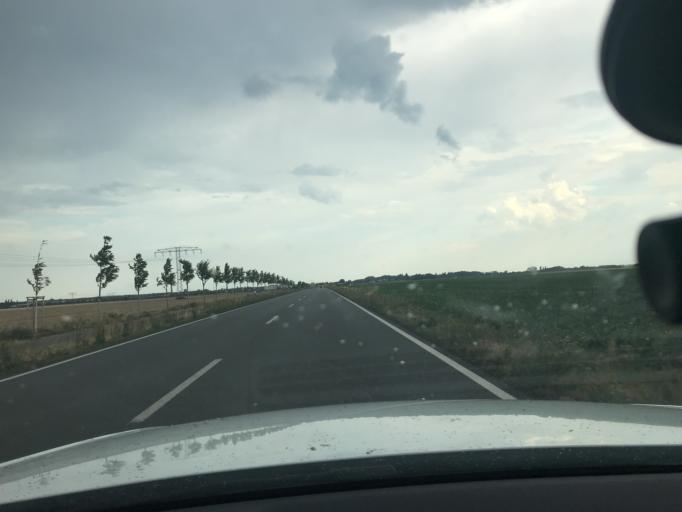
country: DE
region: Saxony
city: Markranstadt
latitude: 51.3233
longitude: 12.2084
